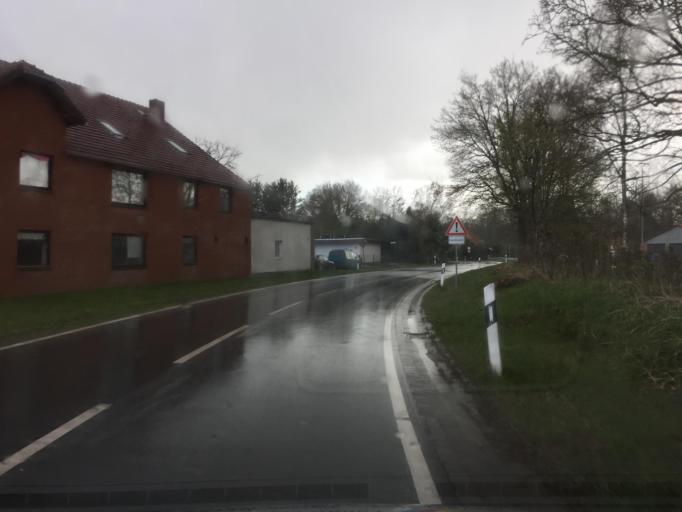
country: DE
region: Lower Saxony
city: Sustedt
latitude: 52.9100
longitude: 8.9071
